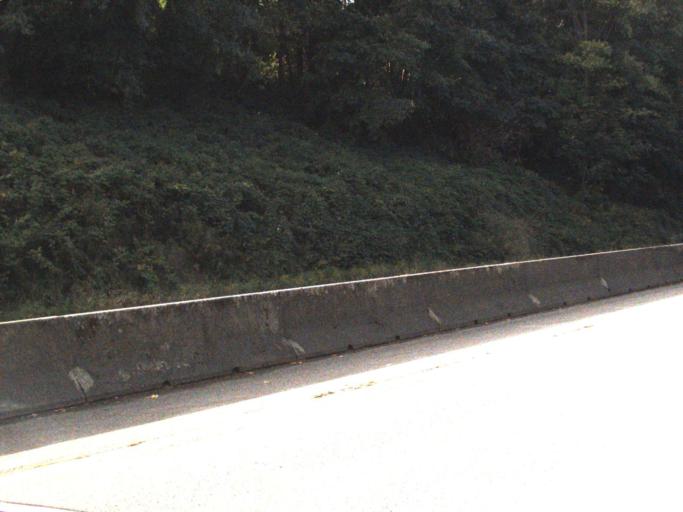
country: US
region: Washington
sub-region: Jefferson County
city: Port Hadlock-Irondale
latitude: 47.9937
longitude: -122.8499
